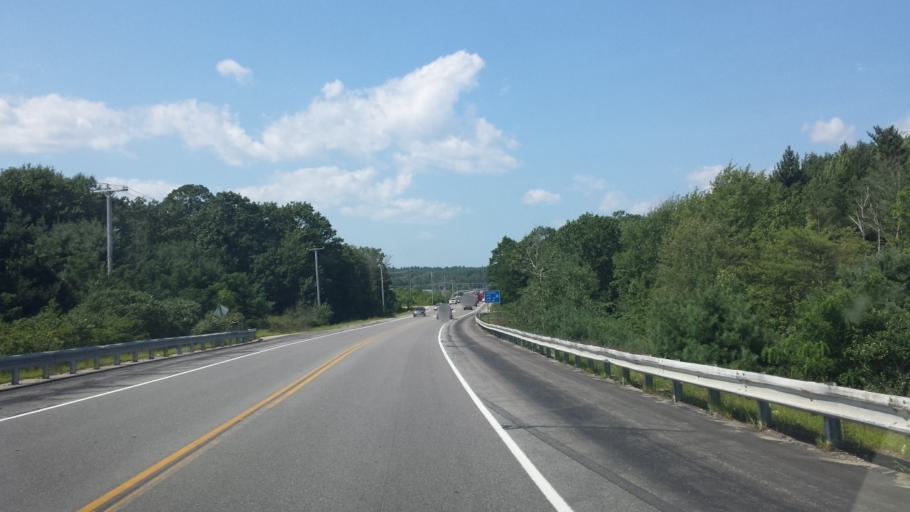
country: US
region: Maine
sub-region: York County
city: Biddeford
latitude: 43.4737
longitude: -70.4924
